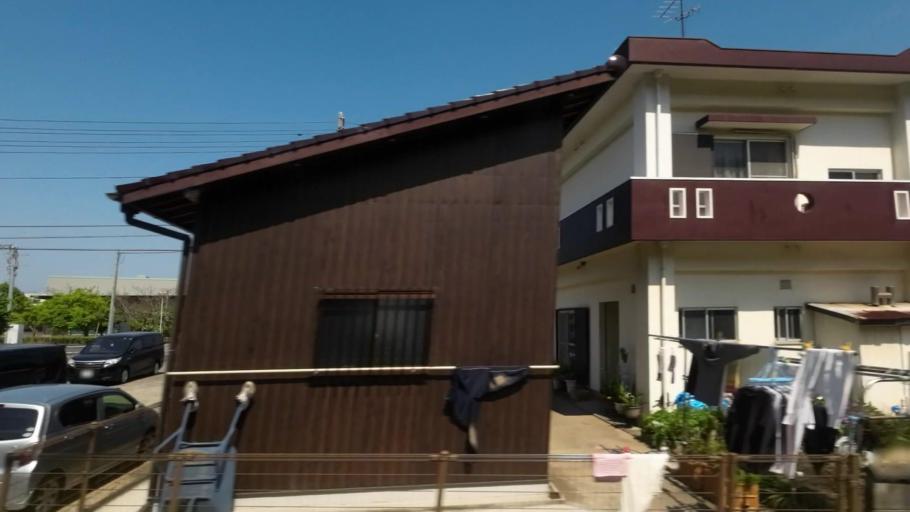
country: JP
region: Ehime
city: Kawanoecho
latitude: 34.0294
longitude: 133.5841
